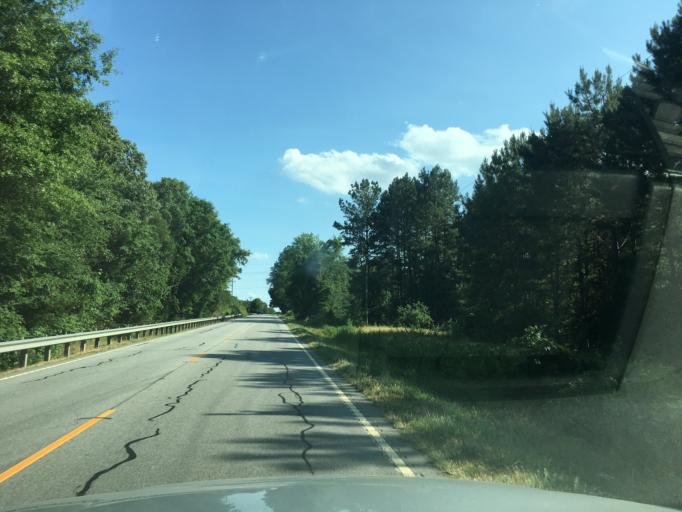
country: US
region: South Carolina
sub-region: Laurens County
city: Watts Mills
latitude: 34.5954
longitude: -81.9151
